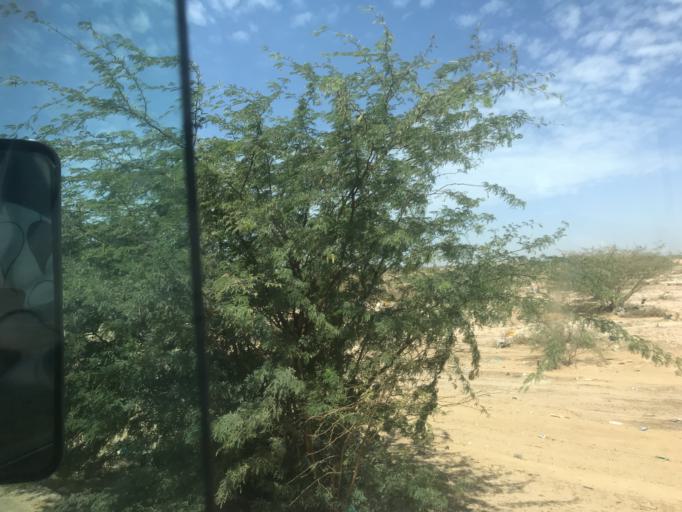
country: SN
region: Saint-Louis
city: Saint-Louis
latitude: 16.0449
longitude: -16.4373
